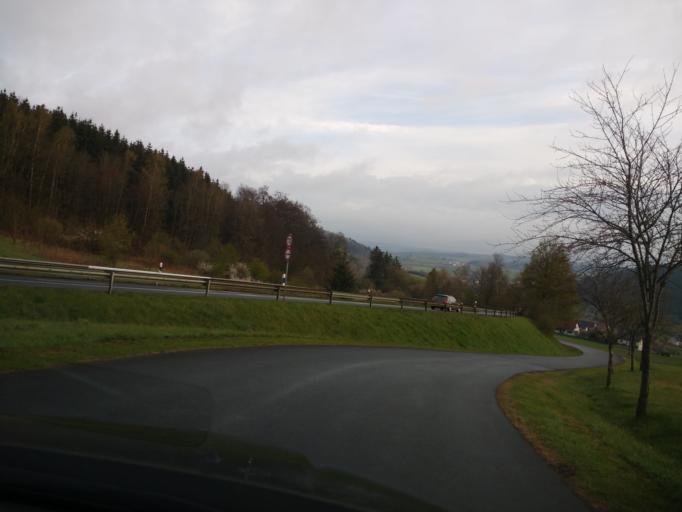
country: DE
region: Rheinland-Pfalz
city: Dohm-Lammersdorf
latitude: 50.2454
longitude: 6.6645
